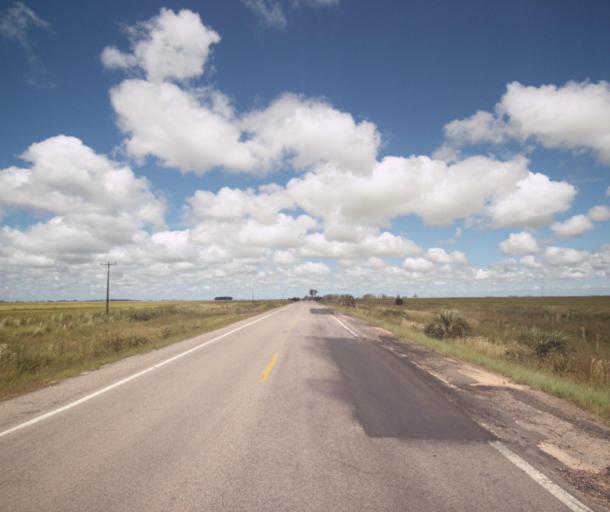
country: BR
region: Rio Grande do Sul
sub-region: Rio Grande
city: Rio Grande
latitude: -32.1680
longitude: -52.4097
